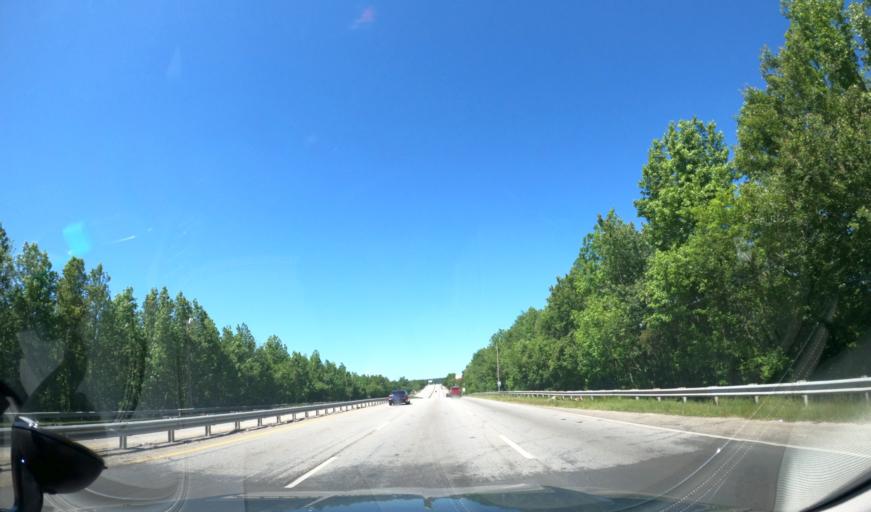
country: US
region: Georgia
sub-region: Richmond County
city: Augusta
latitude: 33.4413
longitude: -81.9862
